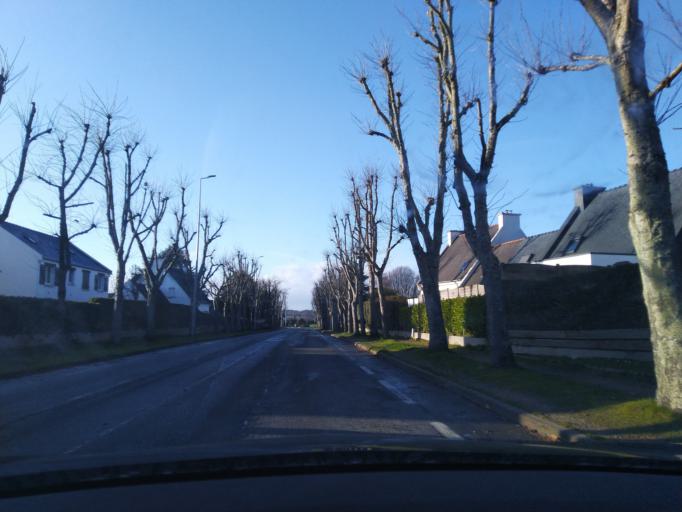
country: FR
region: Brittany
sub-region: Departement du Finistere
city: Morlaix
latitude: 48.5877
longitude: -3.8216
